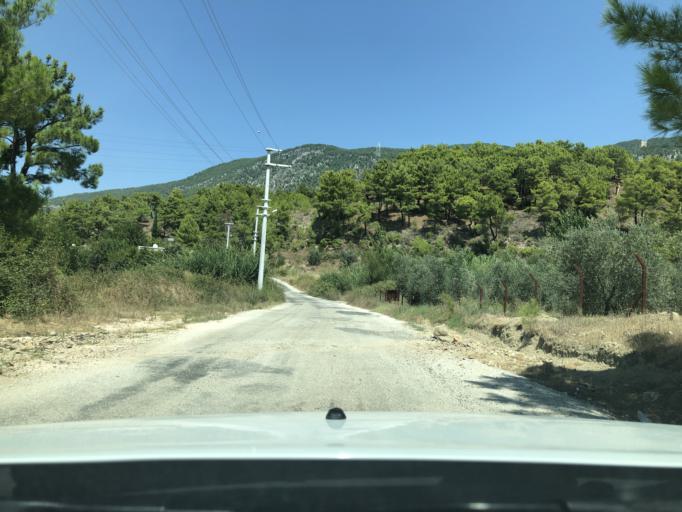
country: TR
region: Antalya
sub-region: Manavgat
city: Kizilagac
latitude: 36.8613
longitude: 31.5641
